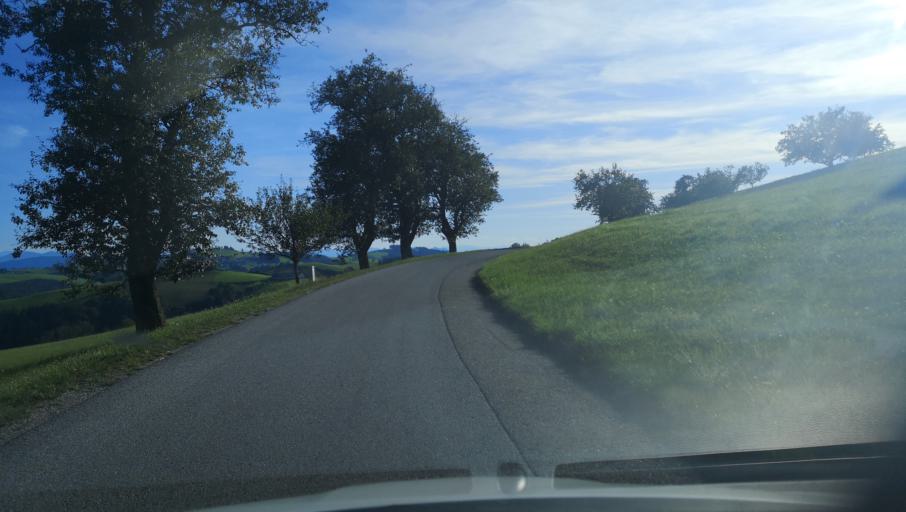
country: AT
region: Lower Austria
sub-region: Politischer Bezirk Amstetten
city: Neuhofen an der Ybbs
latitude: 48.0187
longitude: 14.9018
